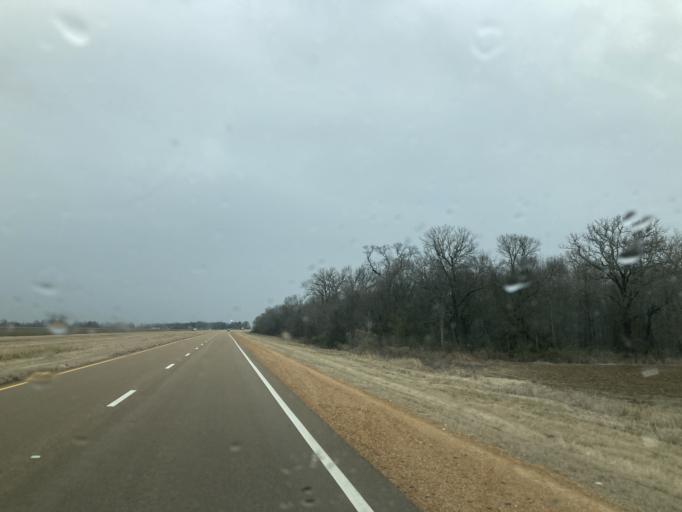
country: US
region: Mississippi
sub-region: Humphreys County
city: Belzoni
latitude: 33.0798
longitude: -90.4812
